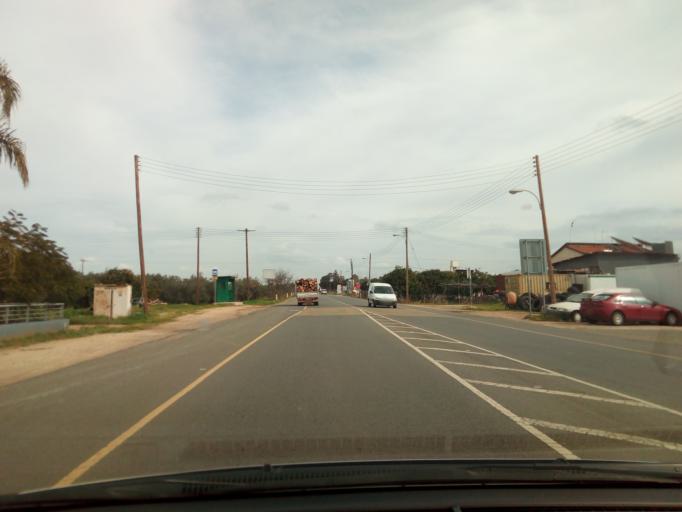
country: CY
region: Lefkosia
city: Peristerona
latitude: 35.1327
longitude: 33.0727
